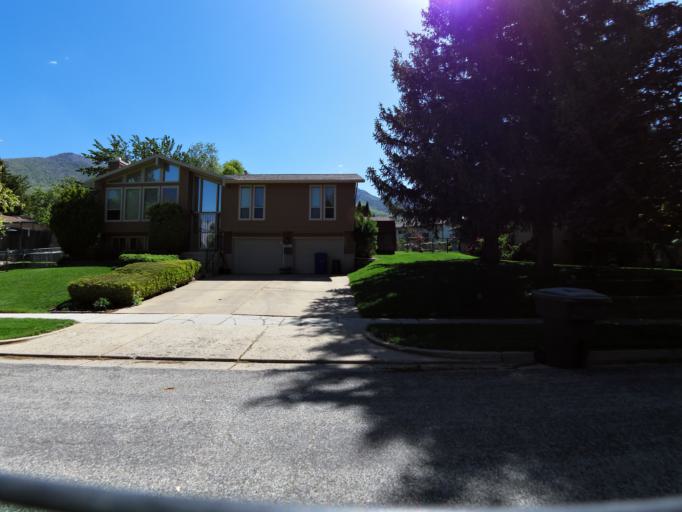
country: US
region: Utah
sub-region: Weber County
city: Uintah
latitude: 41.1716
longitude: -111.9379
